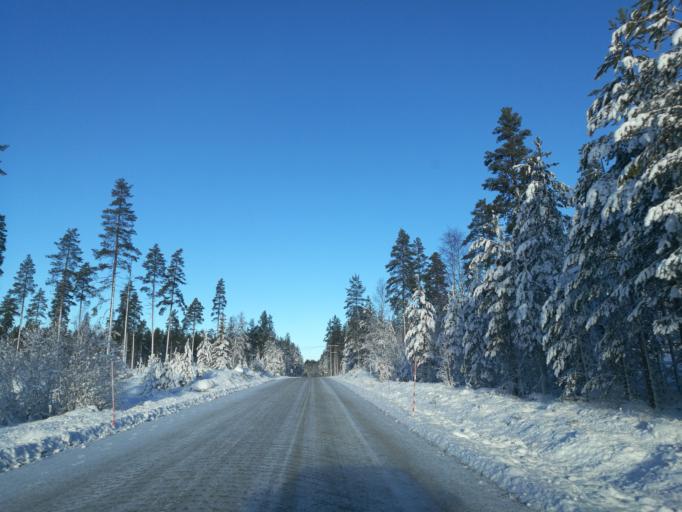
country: NO
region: Hedmark
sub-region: Grue
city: Kirkenaer
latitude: 60.5041
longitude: 12.5585
